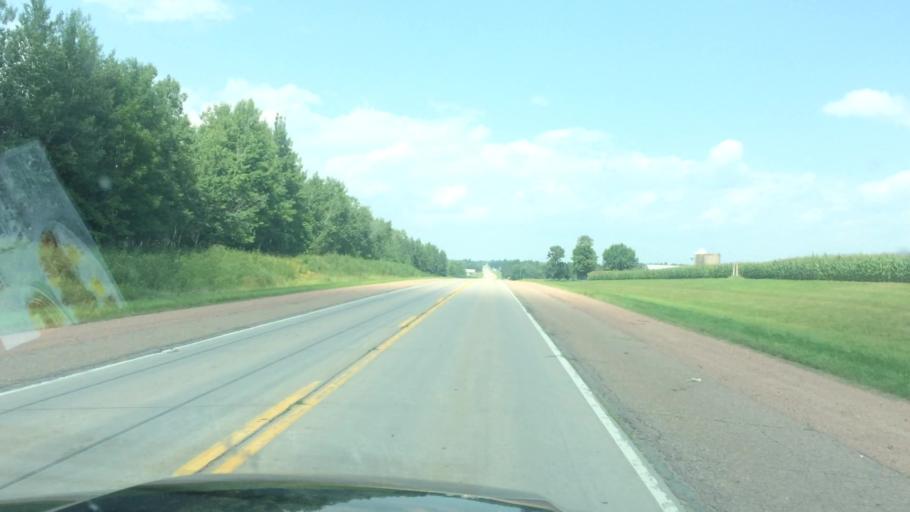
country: US
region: Wisconsin
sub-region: Clark County
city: Colby
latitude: 44.8813
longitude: -90.3155
